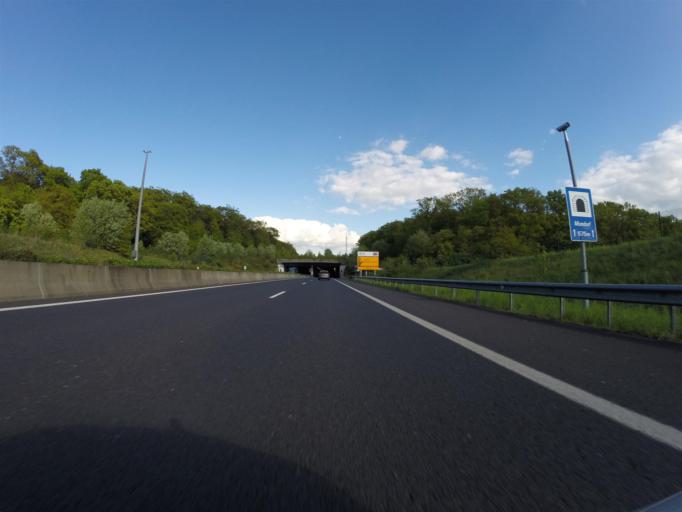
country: LU
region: Grevenmacher
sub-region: Canton de Remich
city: Mondorf-les-Bains
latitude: 49.5180
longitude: 6.2764
